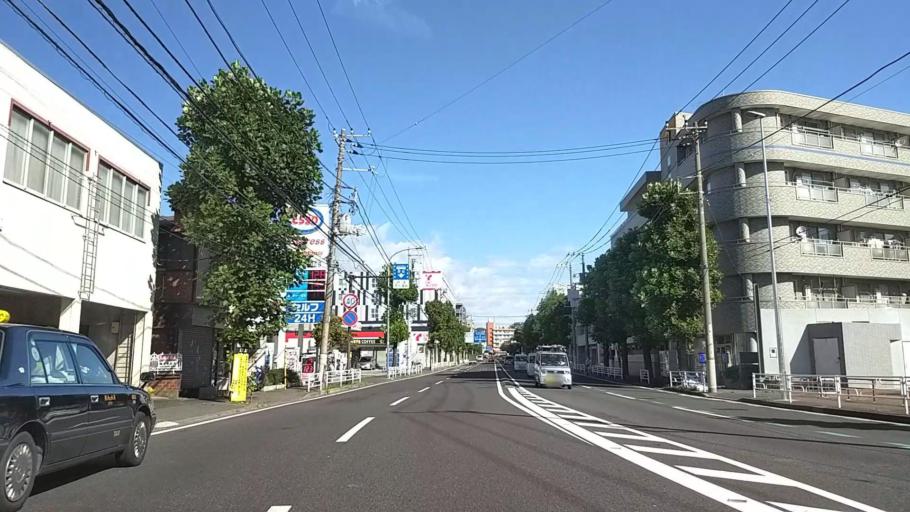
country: JP
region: Kanagawa
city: Yokohama
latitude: 35.4908
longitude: 139.6210
